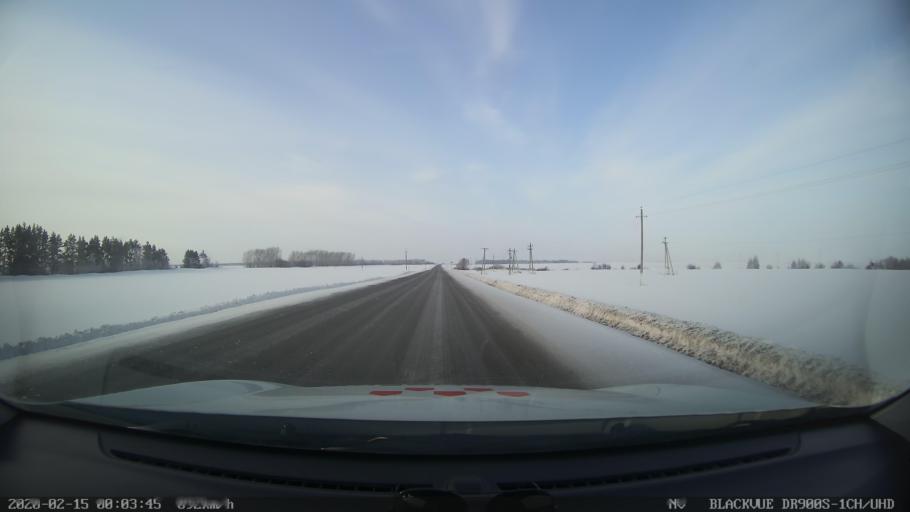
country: RU
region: Tatarstan
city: Kuybyshevskiy Zaton
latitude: 55.3751
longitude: 48.9936
